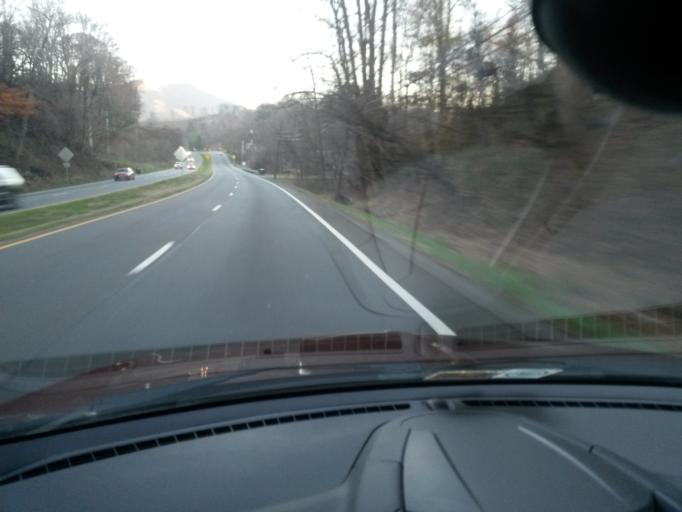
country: US
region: Virginia
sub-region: Roanoke County
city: Narrows
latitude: 37.1499
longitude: -79.9611
